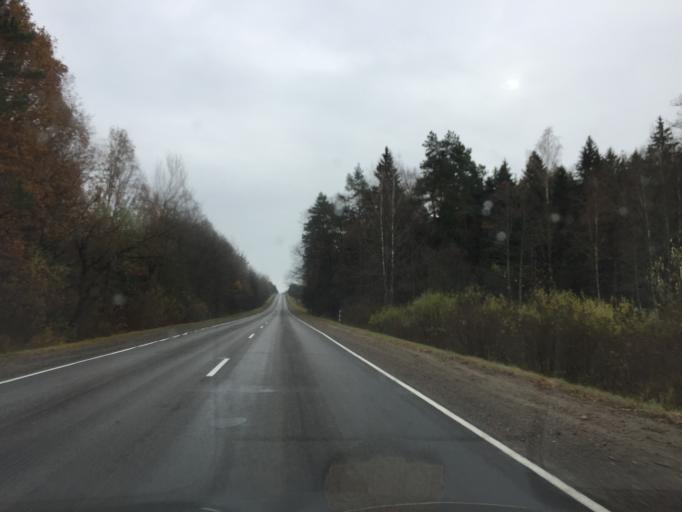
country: BY
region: Mogilev
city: Chavusy
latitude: 53.7707
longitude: 31.0537
